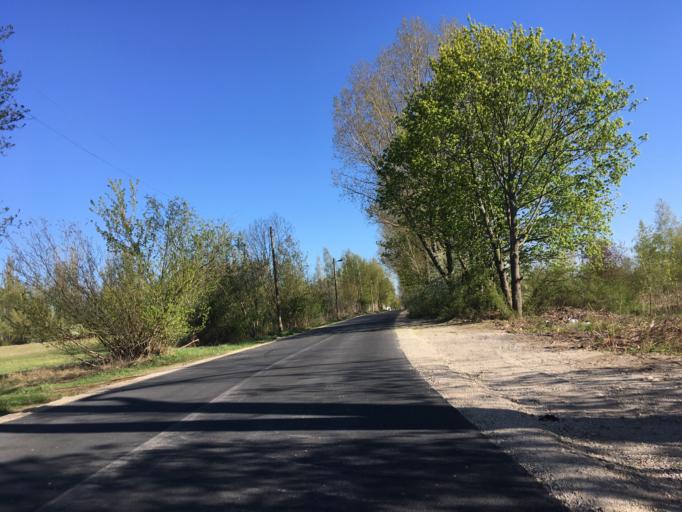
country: DE
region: Berlin
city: Wartenberg
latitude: 52.5791
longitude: 13.4988
